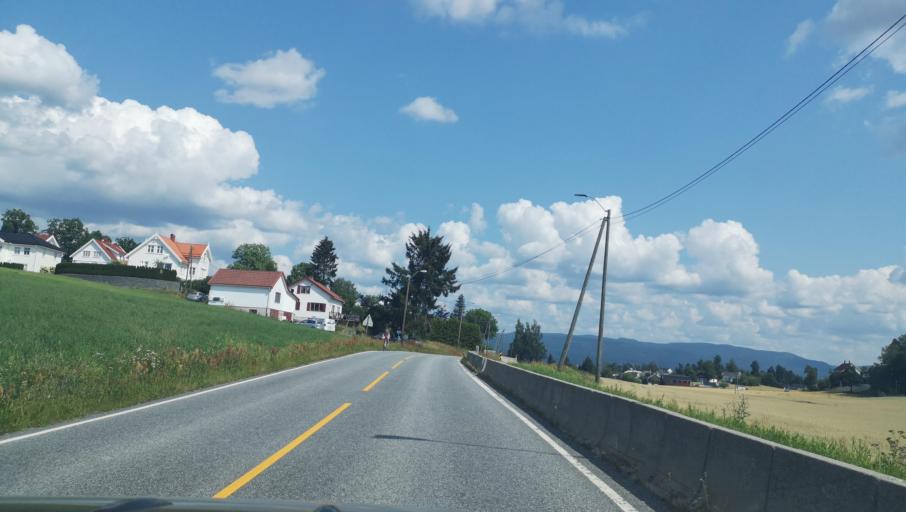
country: NO
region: Buskerud
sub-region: Ovre Eiker
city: Hokksund
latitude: 59.7299
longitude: 9.8434
